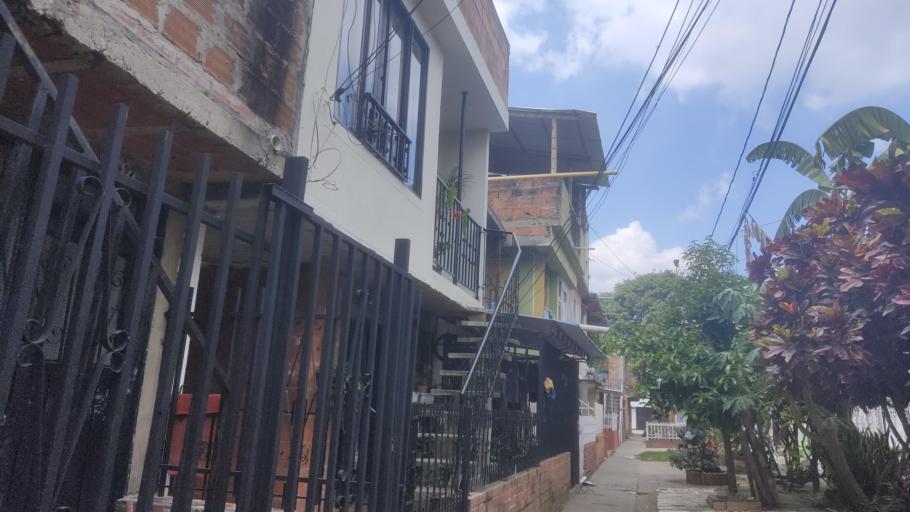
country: CO
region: Valle del Cauca
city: Jamundi
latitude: 3.2489
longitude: -76.5429
